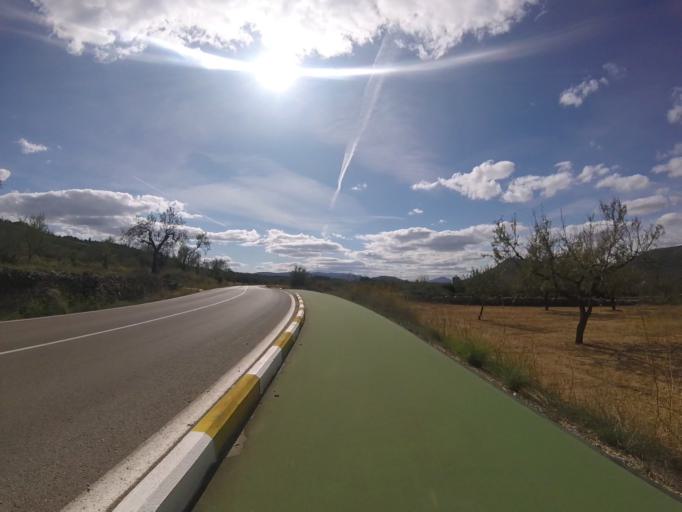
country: ES
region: Valencia
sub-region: Provincia de Castello
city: Cati
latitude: 40.4200
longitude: 0.0729
